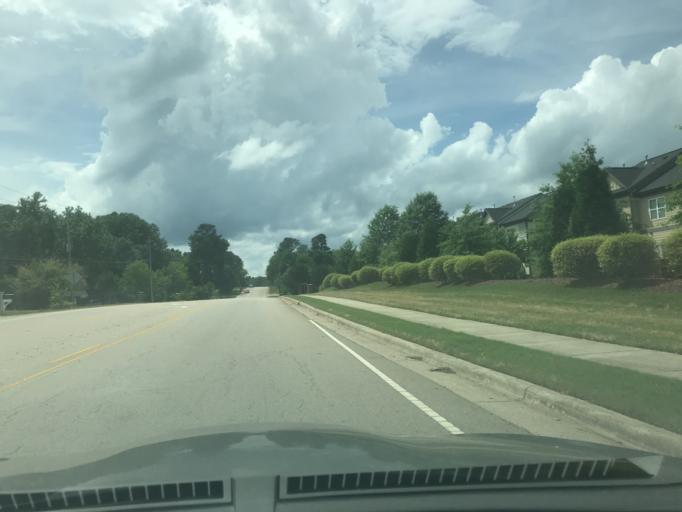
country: US
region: North Carolina
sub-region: Wake County
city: West Raleigh
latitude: 35.8843
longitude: -78.5917
